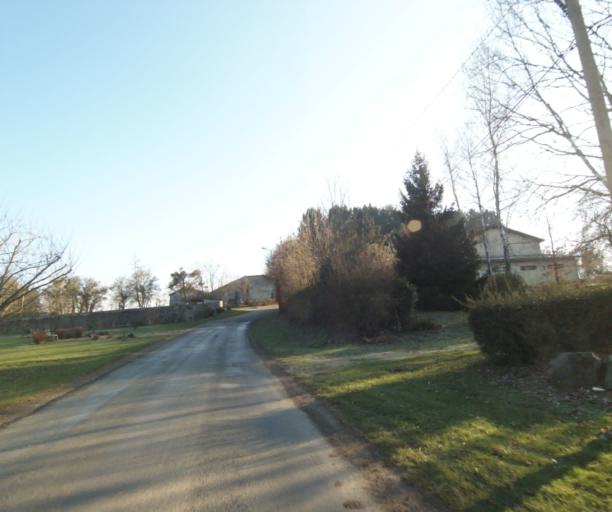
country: FR
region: Champagne-Ardenne
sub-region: Departement de la Haute-Marne
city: Bienville
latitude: 48.5870
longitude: 5.0854
